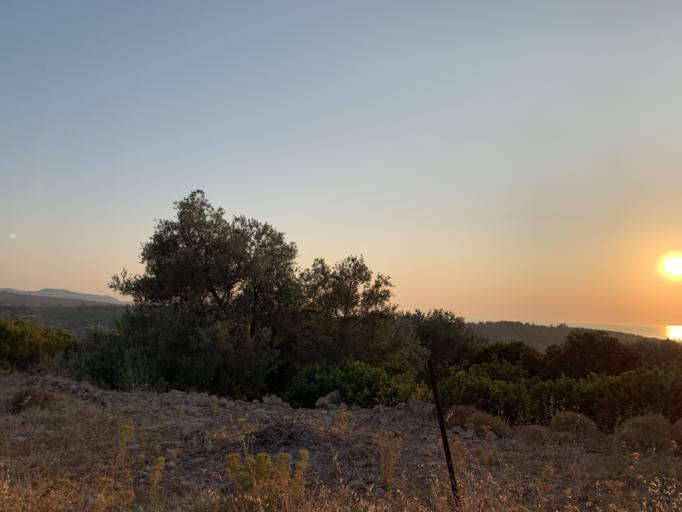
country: GR
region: North Aegean
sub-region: Chios
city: Thymiana
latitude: 38.3411
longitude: 25.9993
